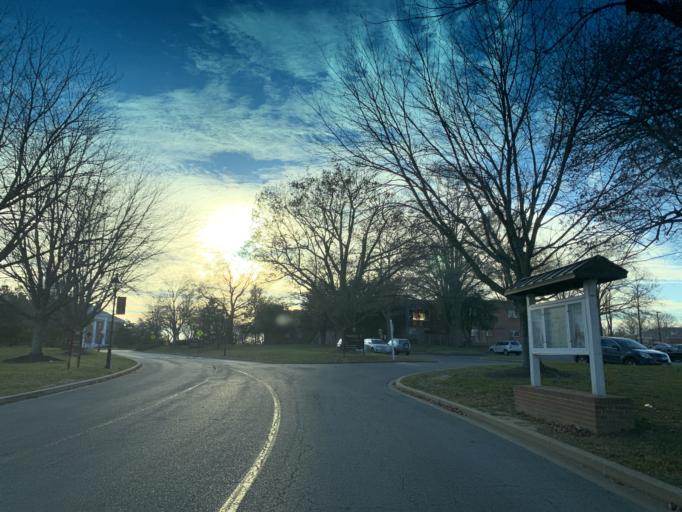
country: US
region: Maryland
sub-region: Kent County
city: Chestertown
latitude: 39.2195
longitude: -76.0681
